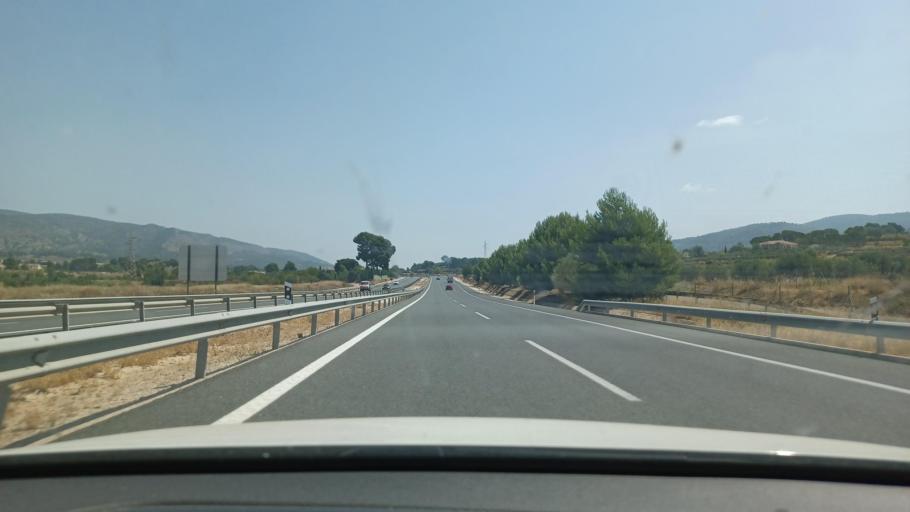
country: ES
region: Valencia
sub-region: Provincia de Alicante
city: Ibi
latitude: 38.6096
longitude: -0.5772
